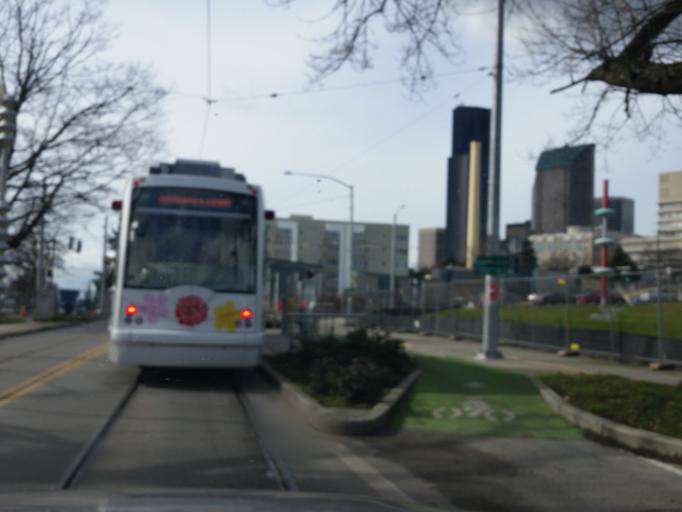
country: US
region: Washington
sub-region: King County
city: Seattle
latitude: 47.6018
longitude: -122.3199
